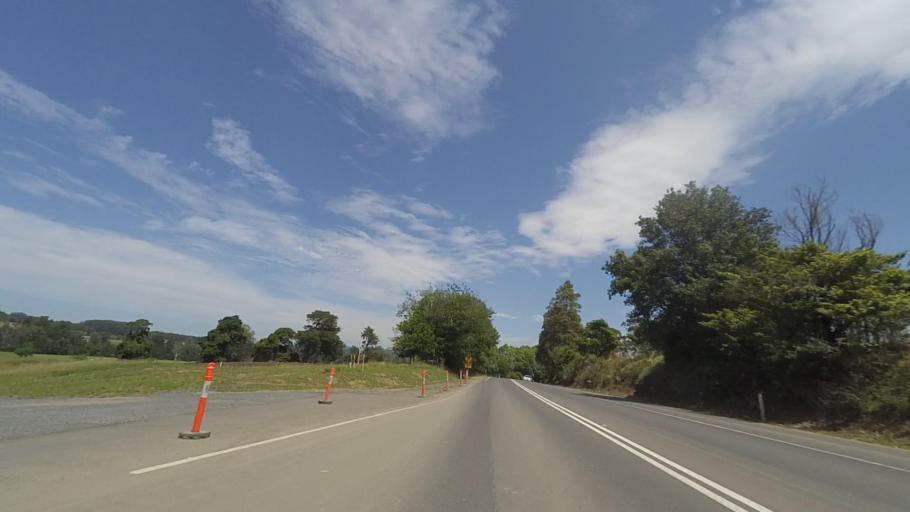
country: AU
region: New South Wales
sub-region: Shoalhaven Shire
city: Berry
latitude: -34.7598
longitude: 150.7402
